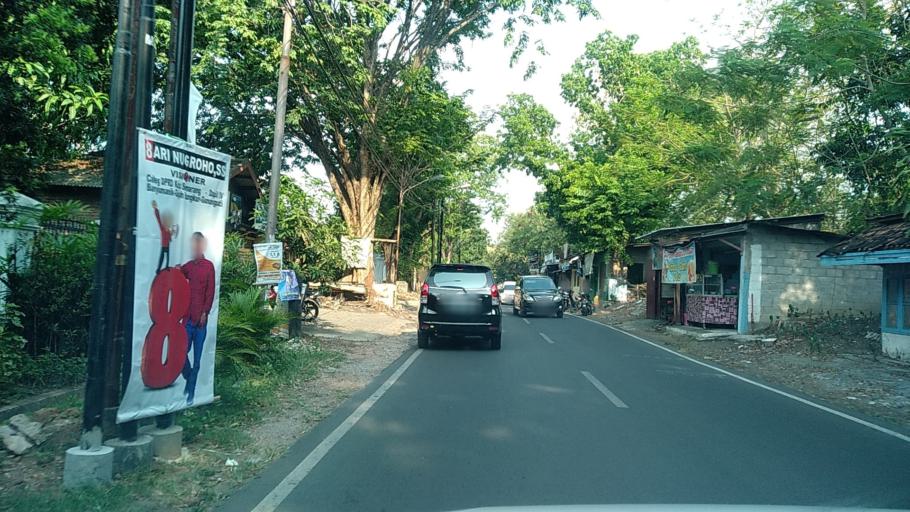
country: ID
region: Central Java
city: Semarang
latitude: -7.0140
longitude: 110.4116
